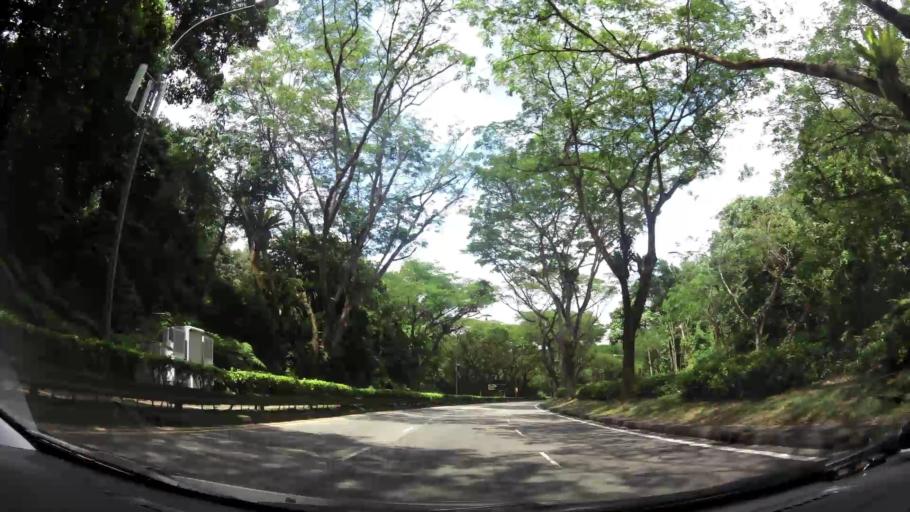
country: MY
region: Johor
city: Johor Bahru
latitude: 1.3888
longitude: 103.8181
